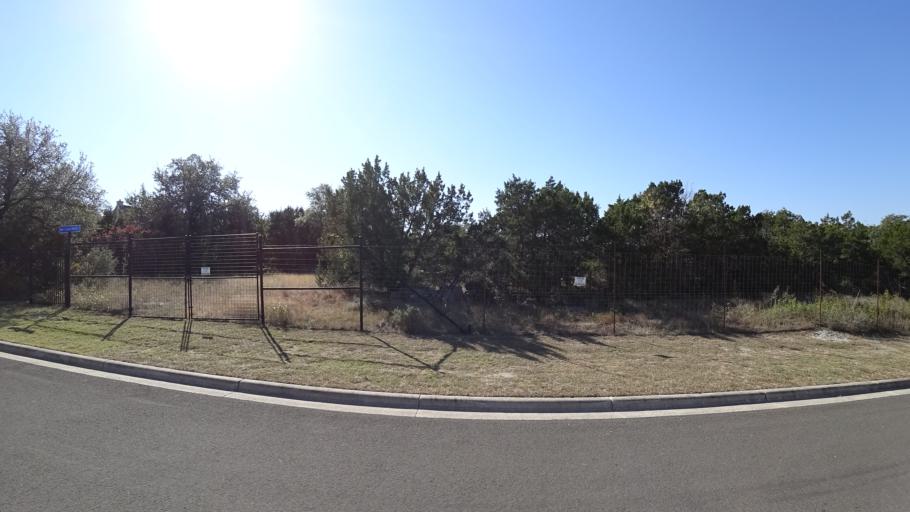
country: US
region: Texas
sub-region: Williamson County
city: Anderson Mill
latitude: 30.3884
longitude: -97.8502
